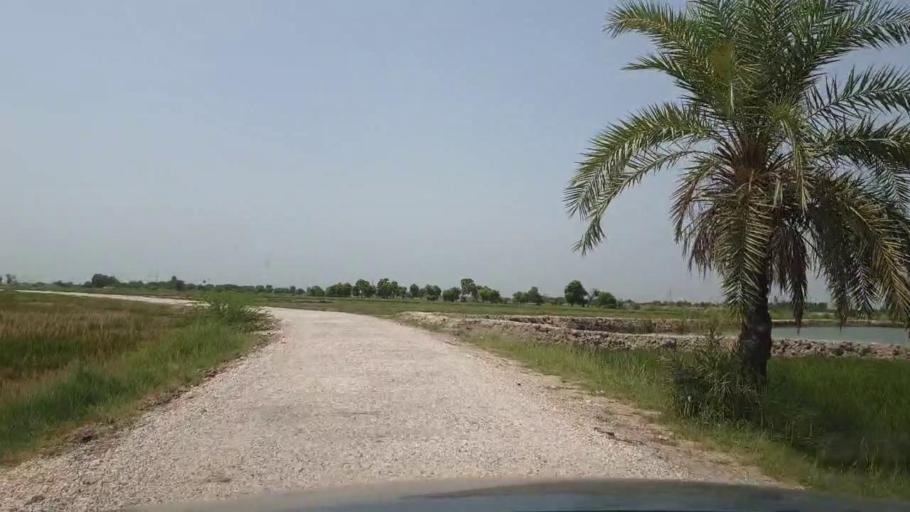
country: PK
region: Sindh
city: Garhi Yasin
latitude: 27.8987
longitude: 68.4990
